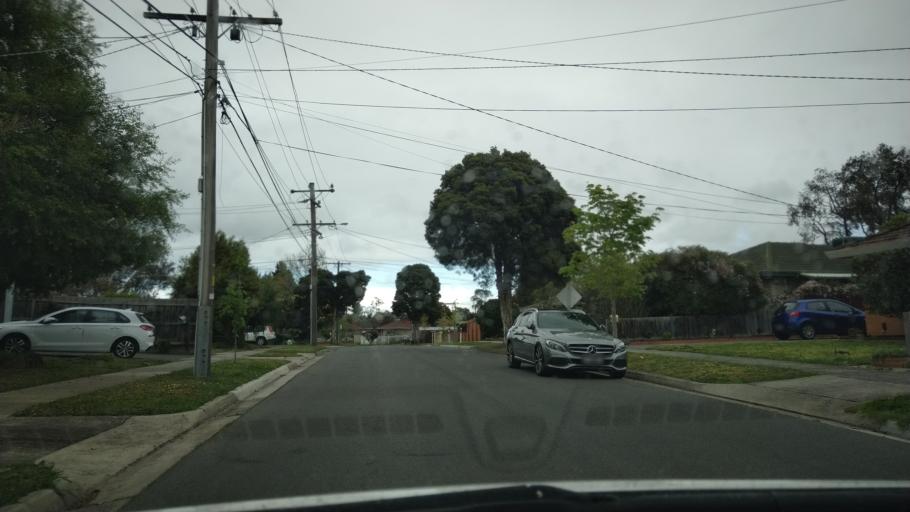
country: AU
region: Victoria
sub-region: Greater Dandenong
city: Keysborough
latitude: -37.9809
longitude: 145.1707
